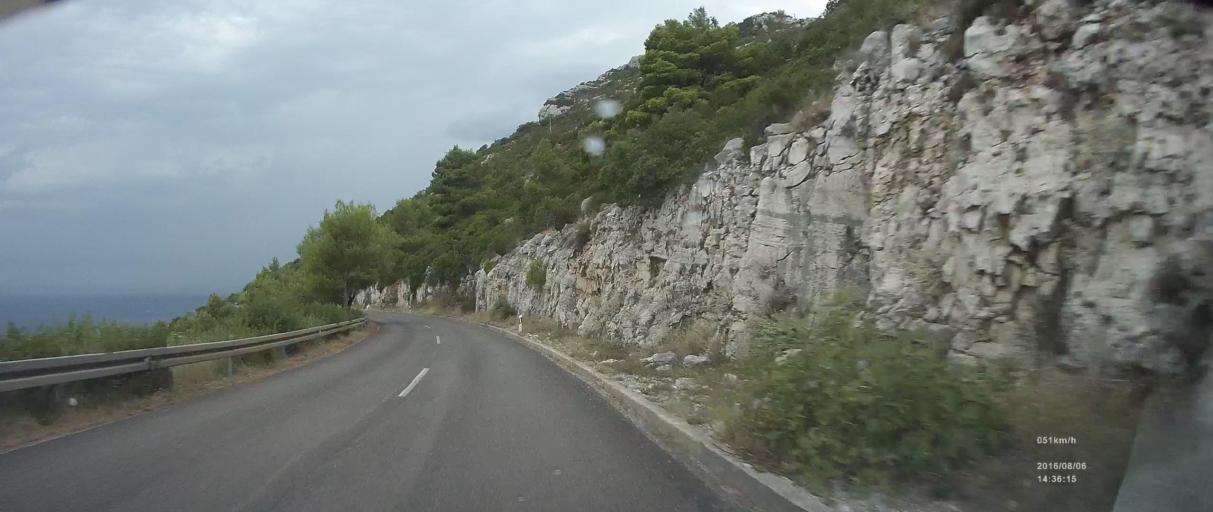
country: HR
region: Dubrovacko-Neretvanska
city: Ston
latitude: 42.7111
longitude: 17.6842
